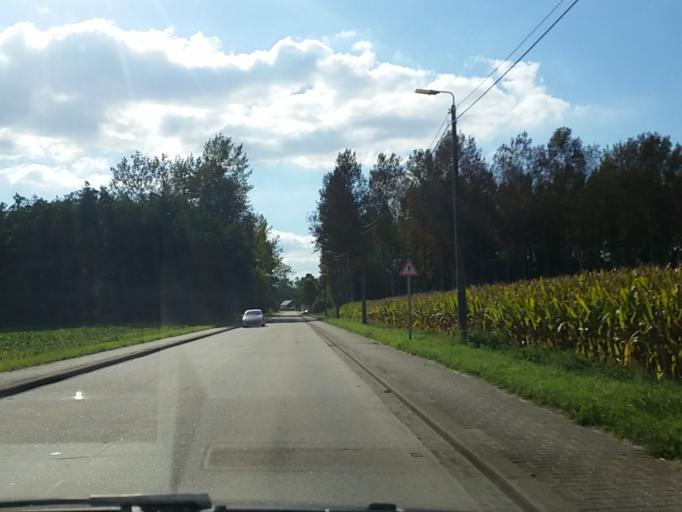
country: BE
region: Flanders
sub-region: Provincie Vlaams-Brabant
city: Rotselaar
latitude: 50.9457
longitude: 4.6986
